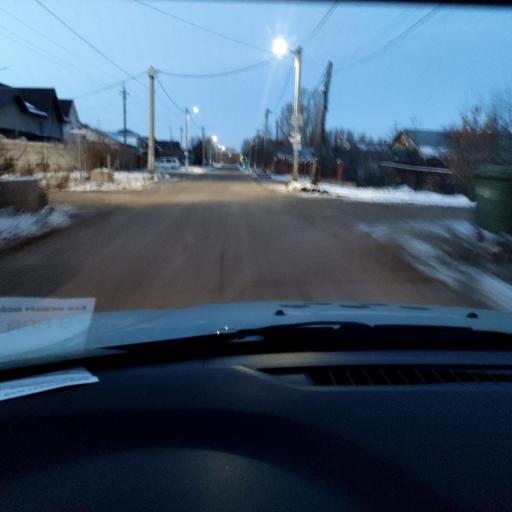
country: RU
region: Samara
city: Tol'yatti
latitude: 53.5664
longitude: 49.3901
